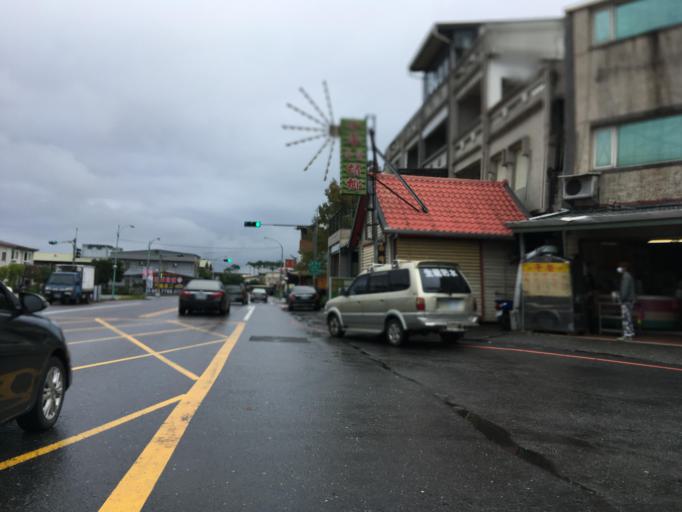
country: TW
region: Taiwan
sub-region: Yilan
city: Yilan
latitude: 24.6563
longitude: 121.7602
